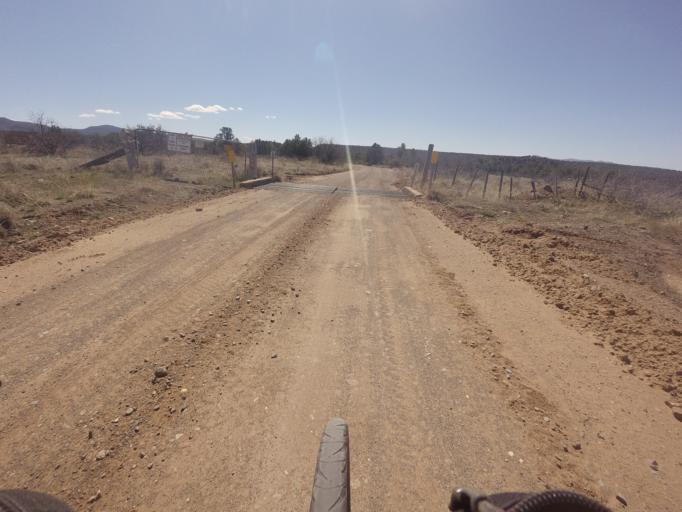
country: US
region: Arizona
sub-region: Yavapai County
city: Lake Montezuma
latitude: 34.6171
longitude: -111.7249
